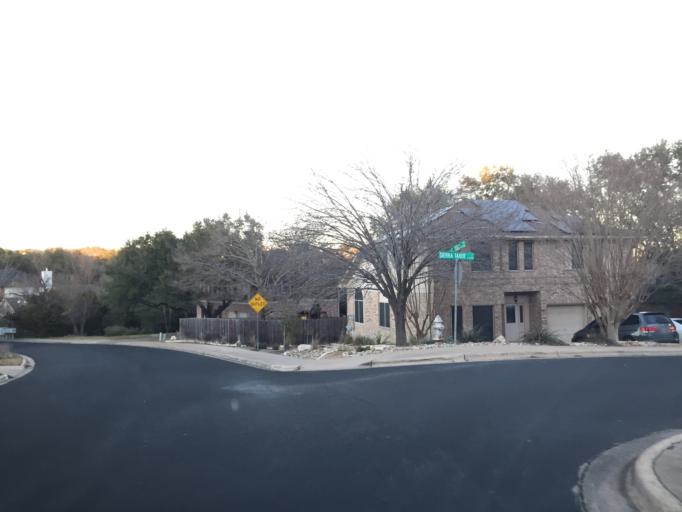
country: US
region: Texas
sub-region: Williamson County
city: Jollyville
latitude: 30.4136
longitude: -97.7645
